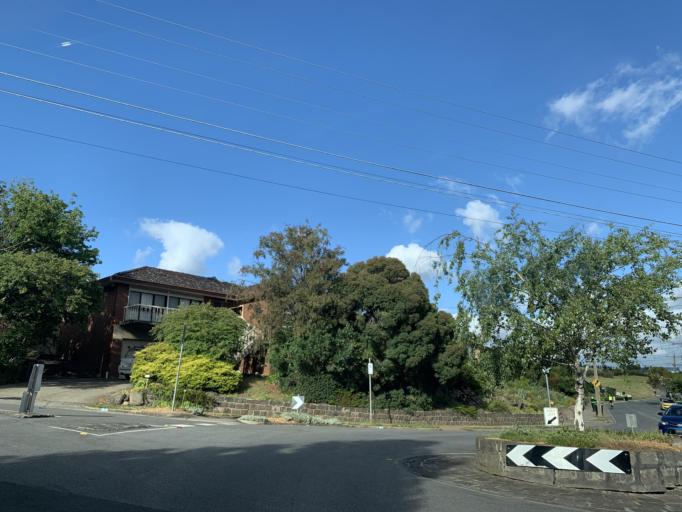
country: AU
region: Victoria
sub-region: Moreland
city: Oak Park
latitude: -37.7190
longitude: 144.9035
